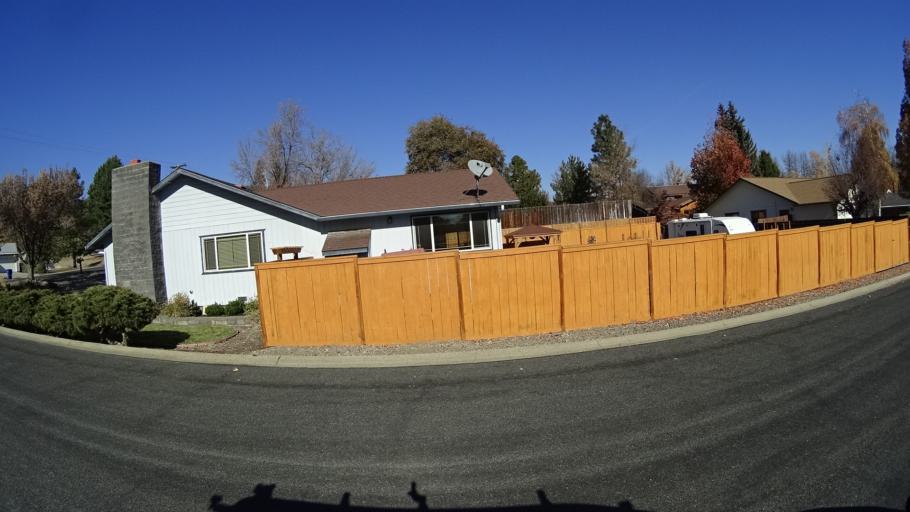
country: US
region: California
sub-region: Siskiyou County
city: Yreka
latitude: 41.7323
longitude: -122.6506
